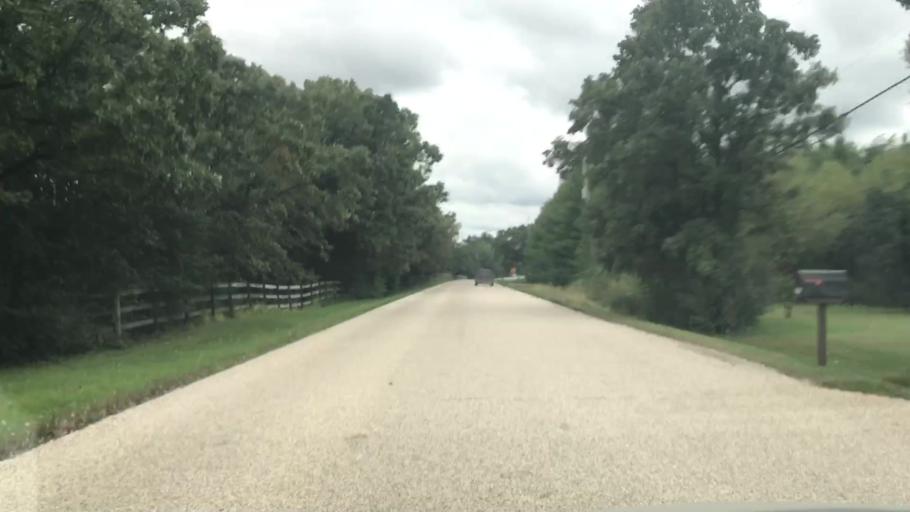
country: US
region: Wisconsin
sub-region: Waukesha County
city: North Prairie
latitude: 42.9186
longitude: -88.4348
